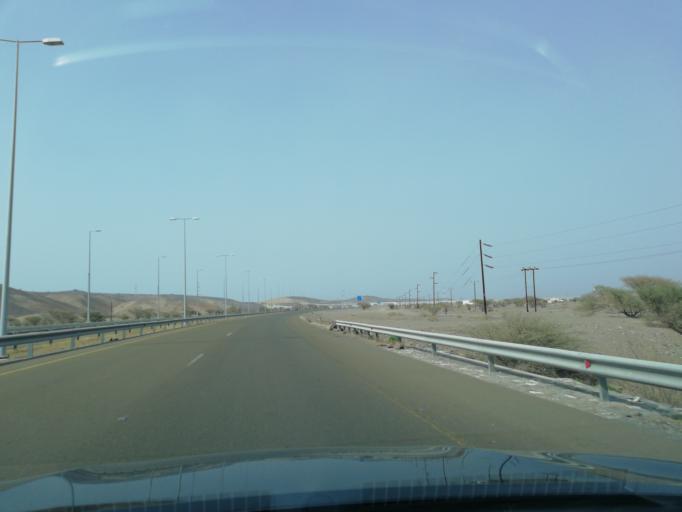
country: OM
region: Al Batinah
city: Al Liwa'
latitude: 24.3743
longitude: 56.5377
